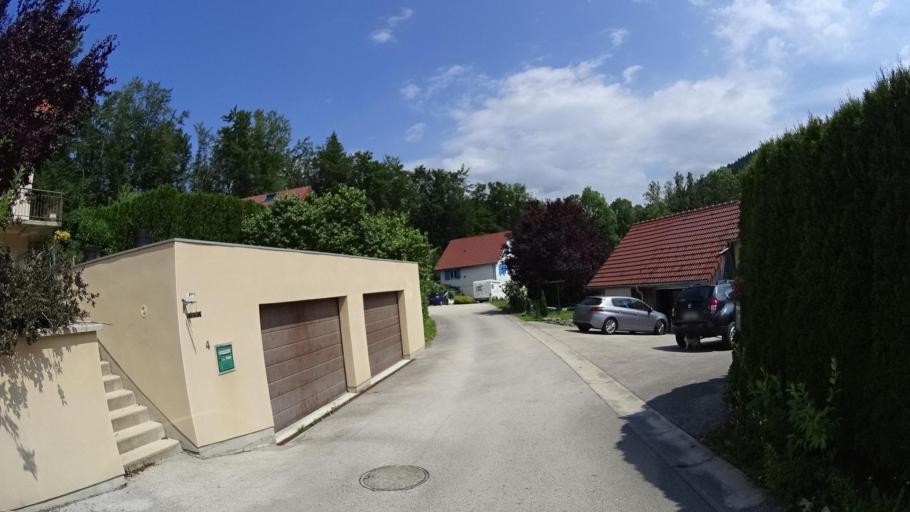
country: FR
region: Franche-Comte
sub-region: Departement du Doubs
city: Les Fourgs
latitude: 46.8195
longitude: 6.3288
